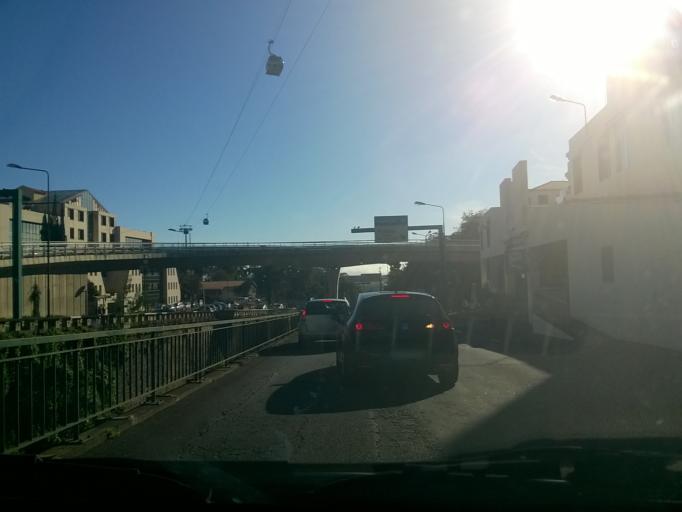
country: PT
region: Madeira
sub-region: Funchal
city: Nossa Senhora do Monte
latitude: 32.6530
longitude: -16.9016
